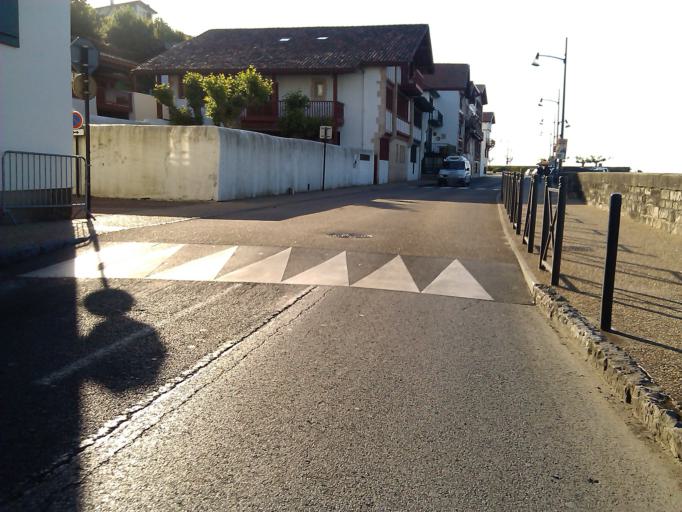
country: FR
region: Aquitaine
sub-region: Departement des Pyrenees-Atlantiques
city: Saint-Jean-de-Luz
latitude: 43.3865
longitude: -1.6685
